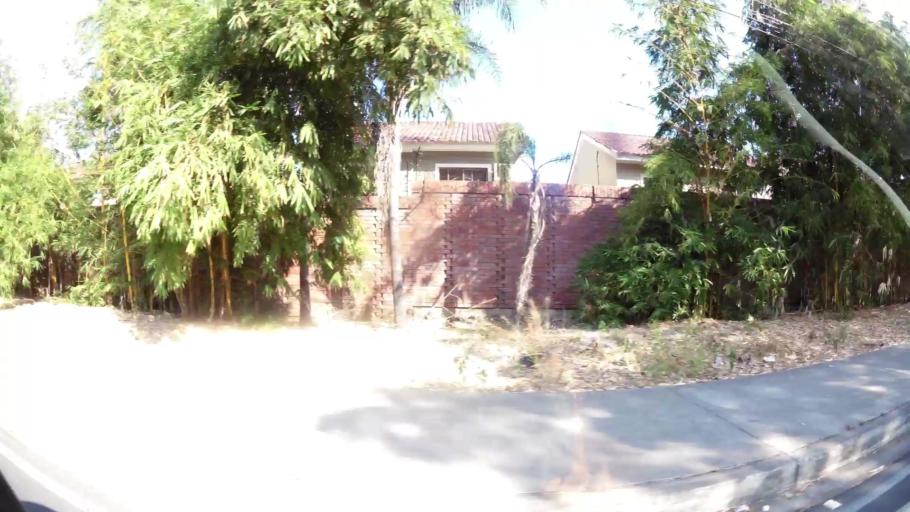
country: EC
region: Guayas
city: Santa Lucia
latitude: -2.1844
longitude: -80.0017
